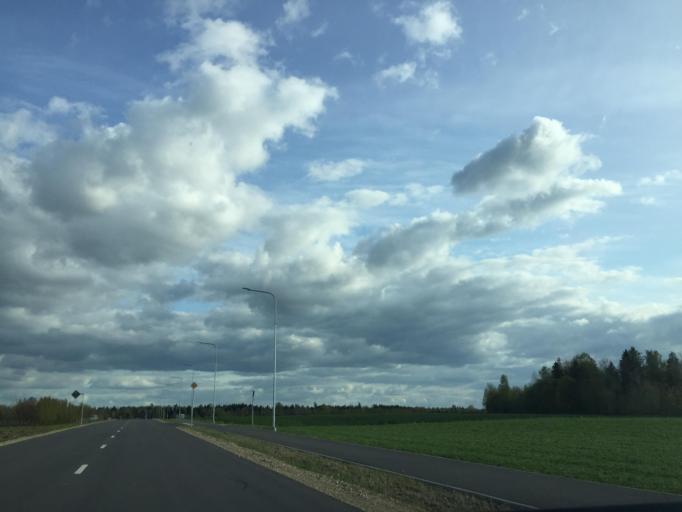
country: LV
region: Sigulda
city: Sigulda
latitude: 57.1380
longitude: 24.8616
